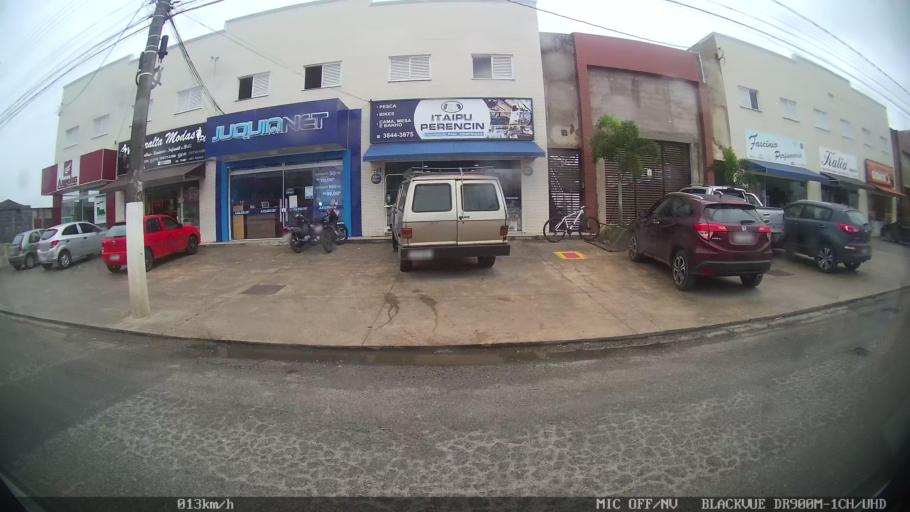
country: BR
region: Sao Paulo
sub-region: Juquia
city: Juquia
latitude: -24.3209
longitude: -47.6370
